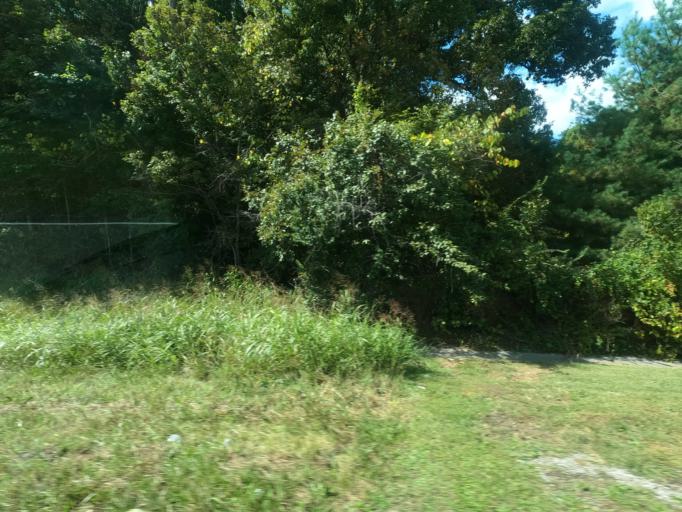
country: US
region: Illinois
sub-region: Johnson County
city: Vienna
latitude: 37.4292
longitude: -88.8929
